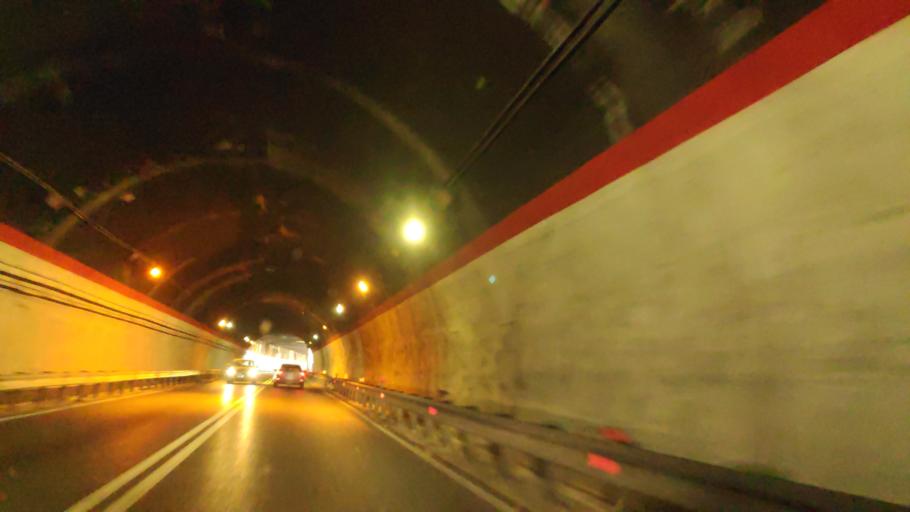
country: IT
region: Calabria
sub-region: Provincia di Catanzaro
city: Squillace Lido
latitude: 38.7643
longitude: 16.5667
